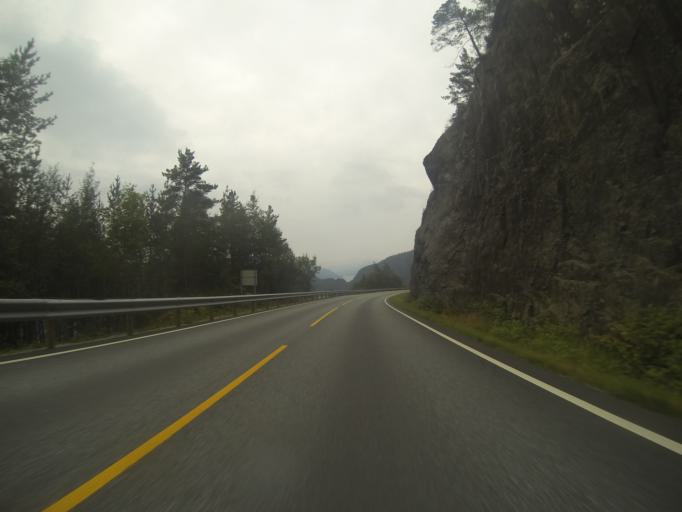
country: NO
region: Rogaland
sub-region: Suldal
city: Sand
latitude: 59.4706
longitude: 6.1827
